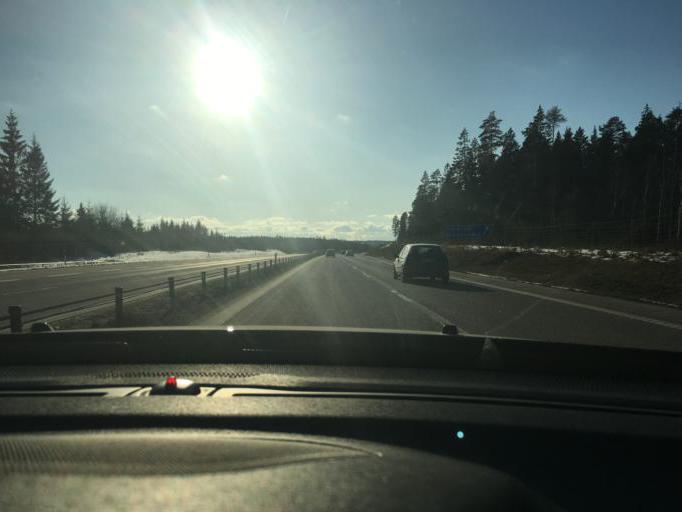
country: SE
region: Vaestra Goetaland
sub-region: Boras Kommun
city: Dalsjofors
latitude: 57.8025
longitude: 13.1663
